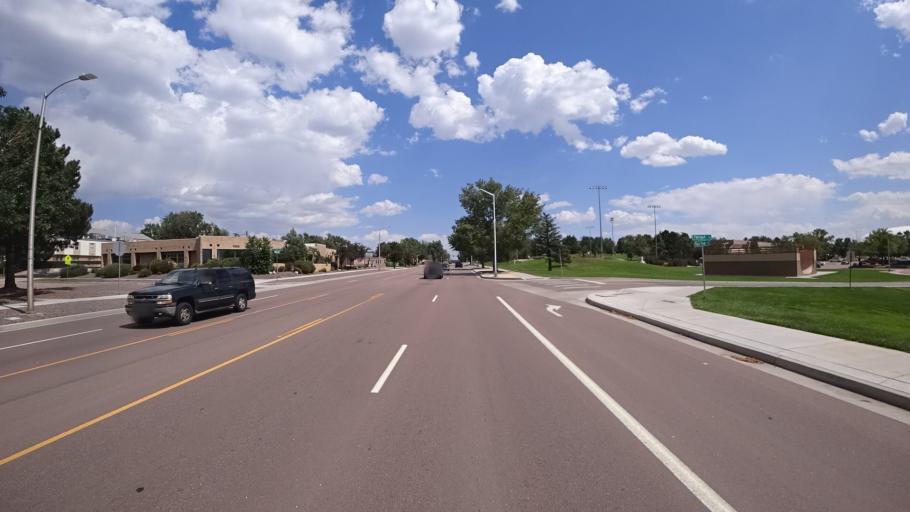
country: US
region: Colorado
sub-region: El Paso County
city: Colorado Springs
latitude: 38.8330
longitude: -104.7981
